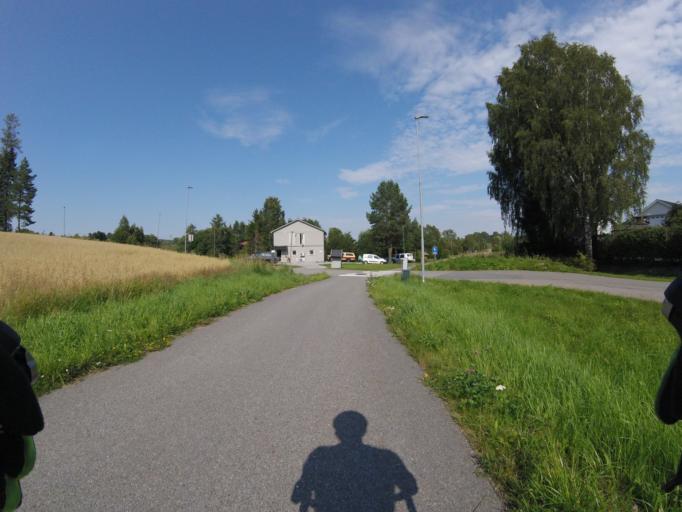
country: NO
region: Akershus
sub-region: Skedsmo
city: Leirsund
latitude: 59.9960
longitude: 11.0852
